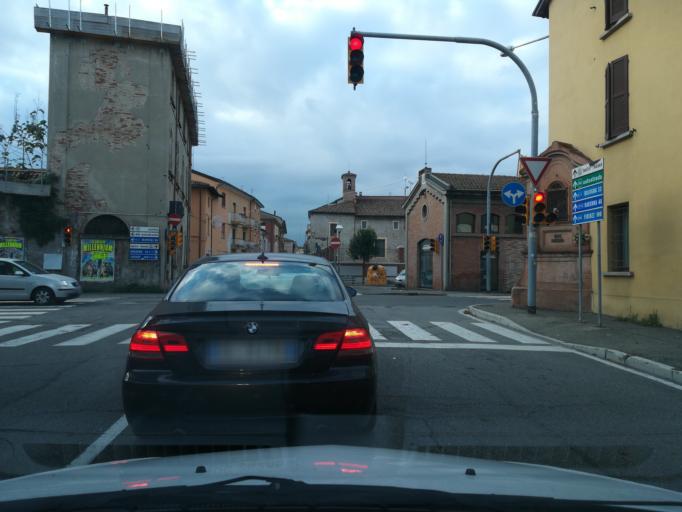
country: IT
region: Emilia-Romagna
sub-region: Provincia di Bologna
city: Imola
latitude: 44.3551
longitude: 11.7187
